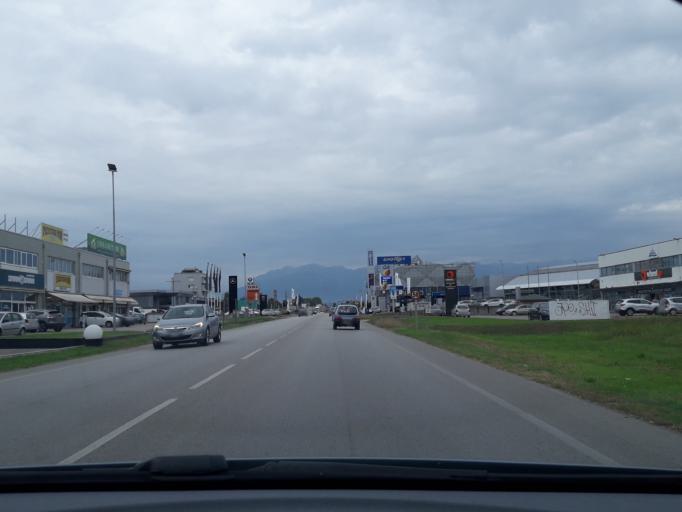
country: IT
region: Friuli Venezia Giulia
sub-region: Provincia di Udine
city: Feletto Umberto
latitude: 46.0997
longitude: 13.2302
